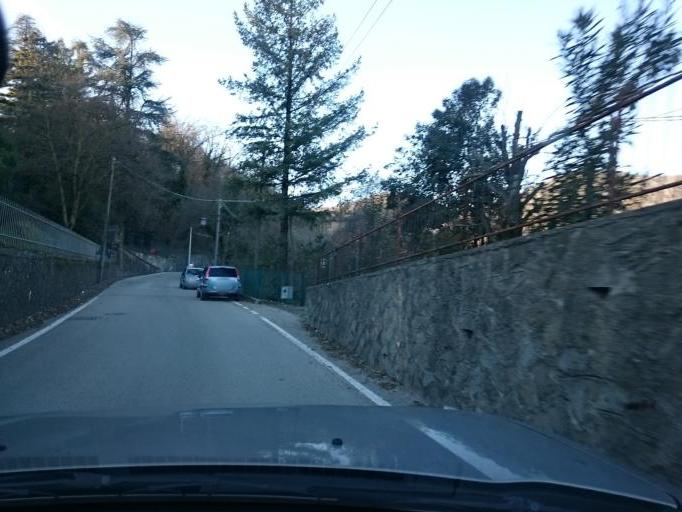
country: IT
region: Veneto
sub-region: Provincia di Padova
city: Vo
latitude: 45.3502
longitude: 11.6725
